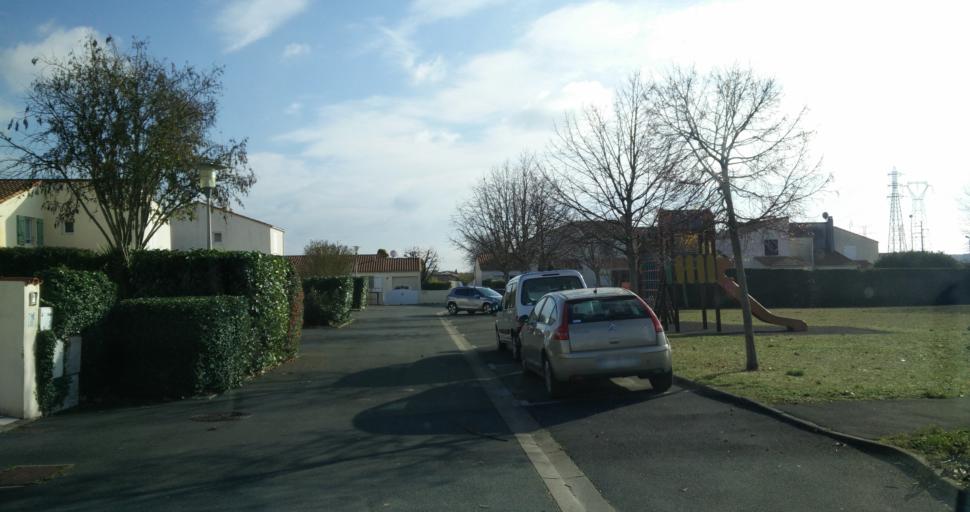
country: FR
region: Poitou-Charentes
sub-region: Departement de la Charente-Maritime
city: Puilboreau
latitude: 46.1838
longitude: -1.1214
